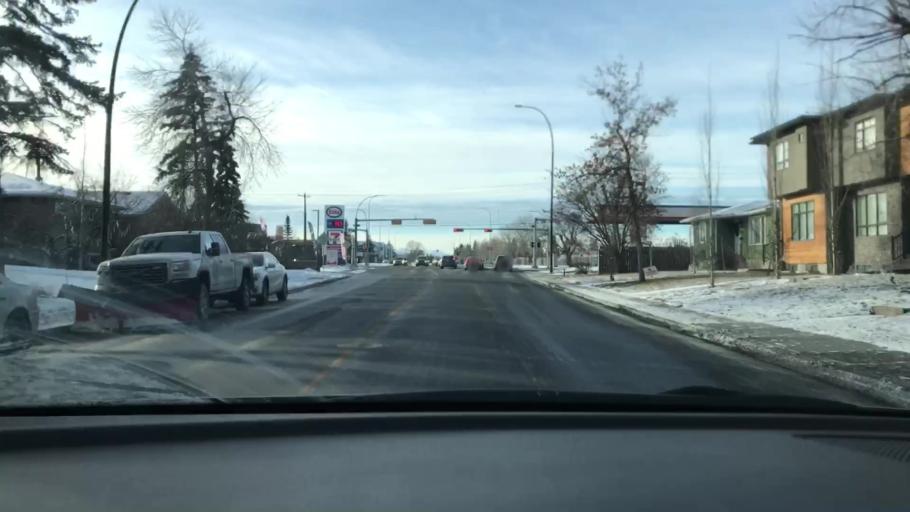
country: CA
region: Alberta
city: Calgary
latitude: 51.0229
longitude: -114.1396
